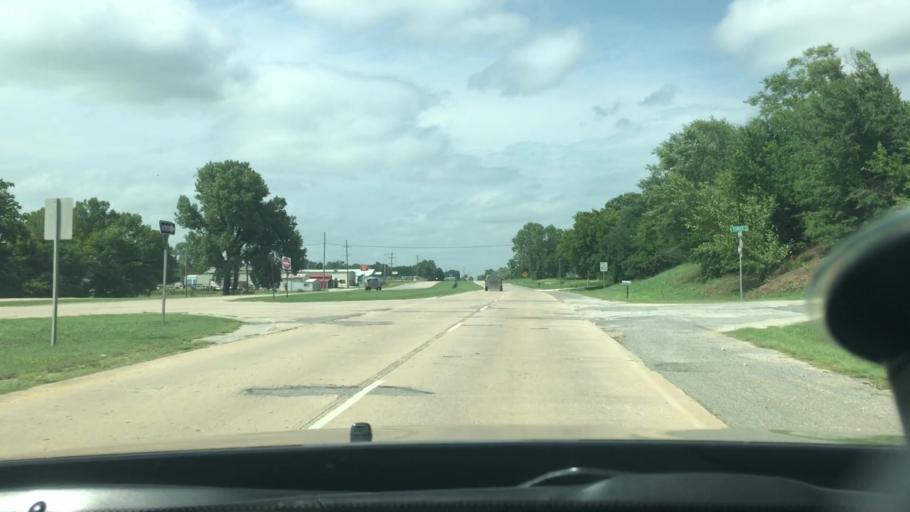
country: US
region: Oklahoma
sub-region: Pontotoc County
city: Ada
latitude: 34.8105
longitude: -96.6782
